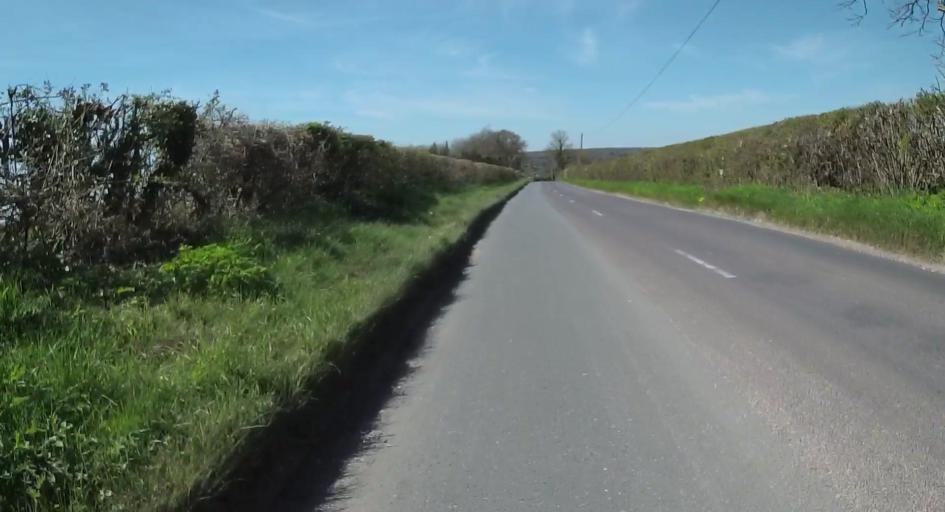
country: GB
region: England
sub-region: Hampshire
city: Winchester
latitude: 51.1032
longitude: -1.3716
